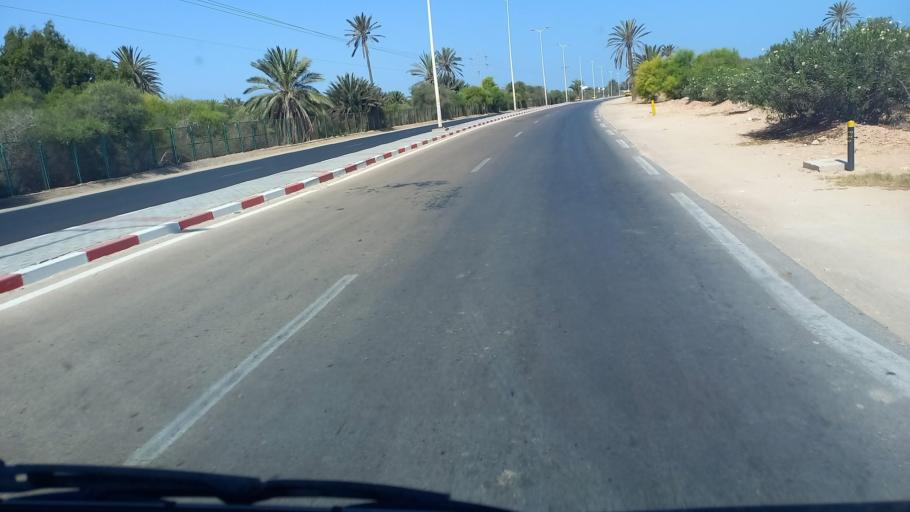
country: TN
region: Madanin
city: Midoun
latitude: 33.8291
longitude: 11.0091
